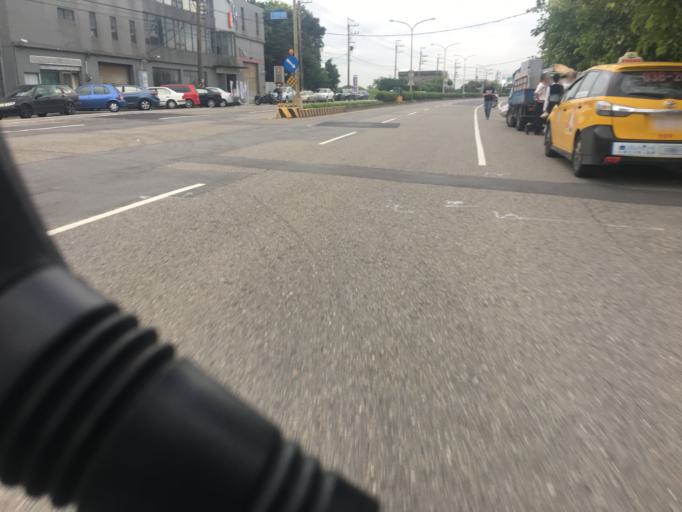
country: TW
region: Taiwan
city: Taoyuan City
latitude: 25.0903
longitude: 121.2293
